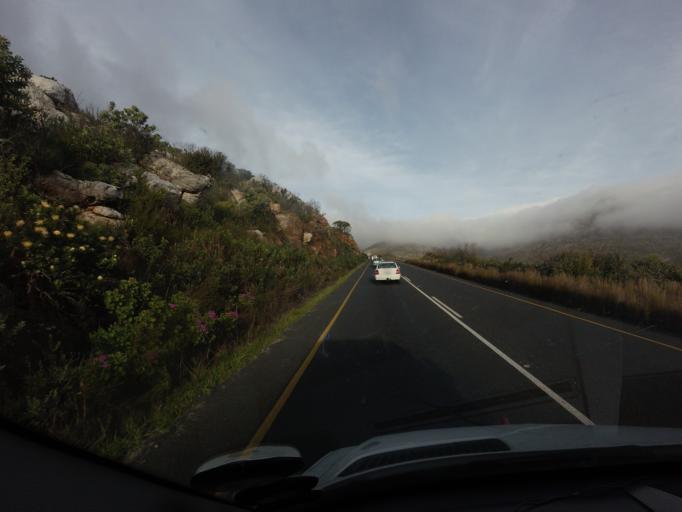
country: ZA
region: Western Cape
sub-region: City of Cape Town
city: Bergvliet
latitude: -34.1015
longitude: 18.4159
